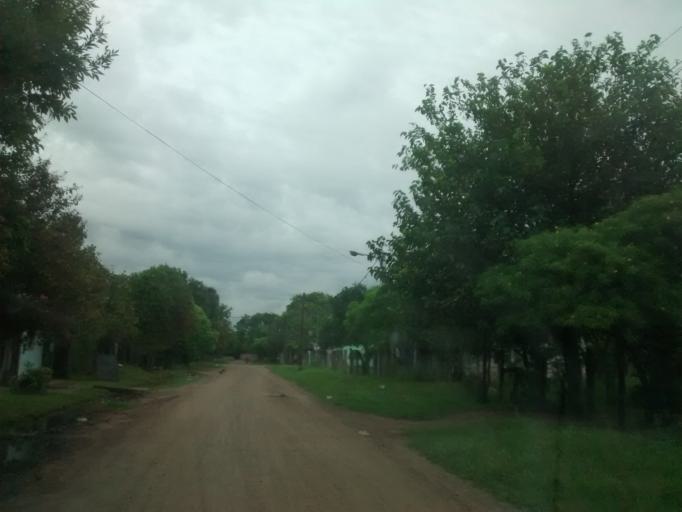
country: AR
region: Chaco
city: Puerto Tirol
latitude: -27.3757
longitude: -59.0967
